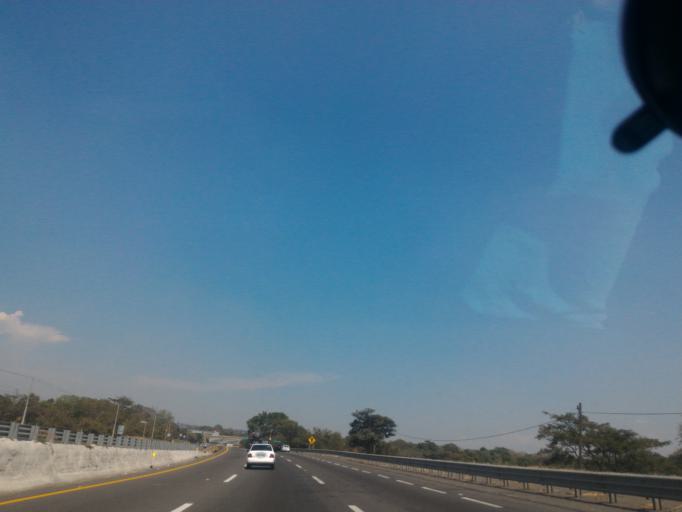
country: MX
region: Colima
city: Cuauhtemoc
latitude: 19.2874
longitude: -103.6548
